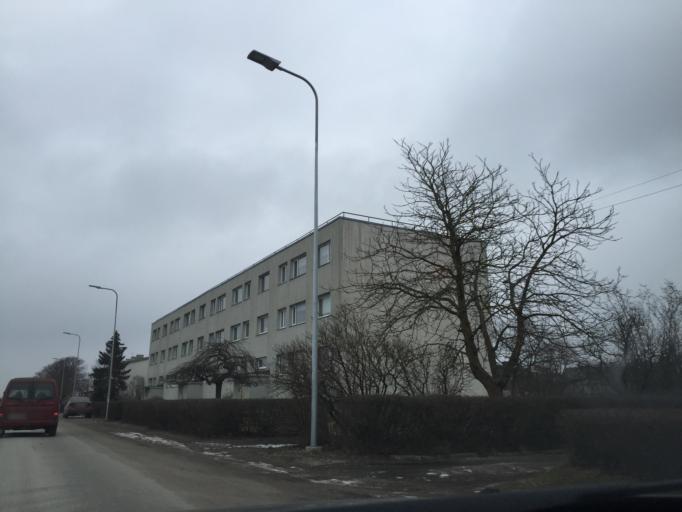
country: EE
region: Saare
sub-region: Kuressaare linn
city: Kuressaare
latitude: 58.2585
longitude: 22.4791
